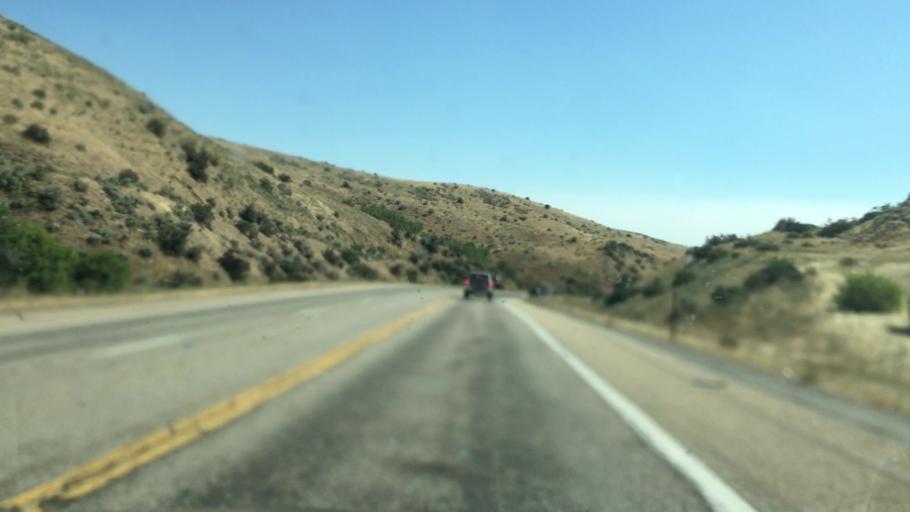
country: US
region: Idaho
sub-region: Ada County
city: Eagle
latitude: 43.8216
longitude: -116.2565
